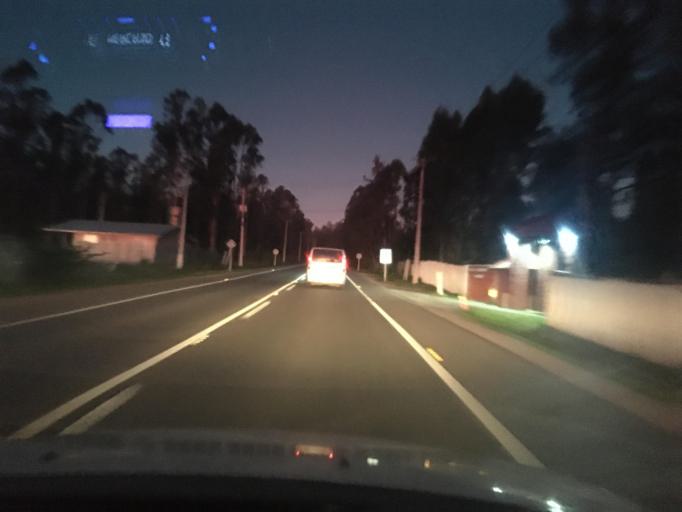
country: CL
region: Valparaiso
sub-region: San Antonio Province
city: El Tabo
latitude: -33.4255
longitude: -71.6699
